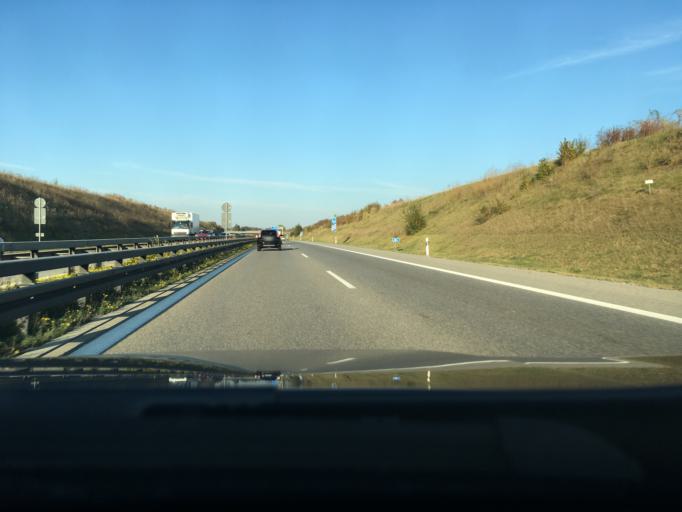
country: DE
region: Baden-Wuerttemberg
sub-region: Tuebingen Region
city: Kisslegg
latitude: 47.7478
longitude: 9.9010
